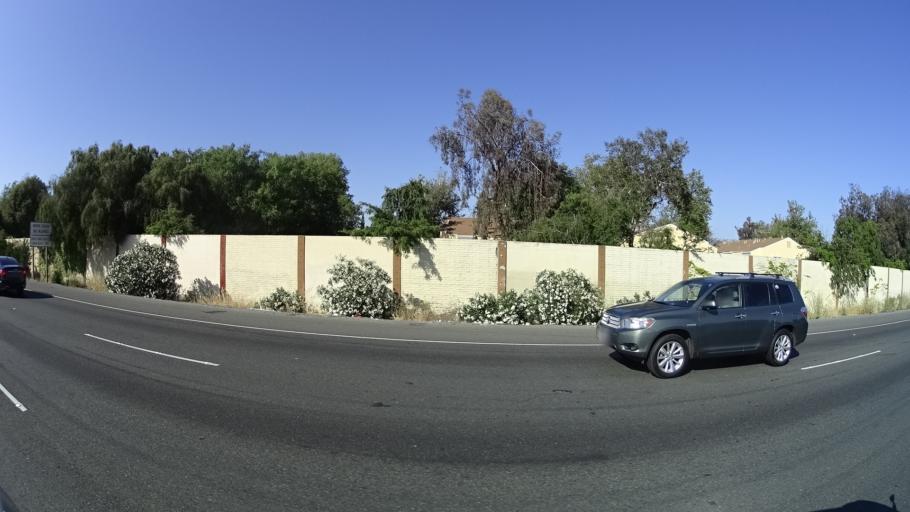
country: US
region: California
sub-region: Santa Clara County
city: Seven Trees
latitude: 37.3240
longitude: -121.8367
